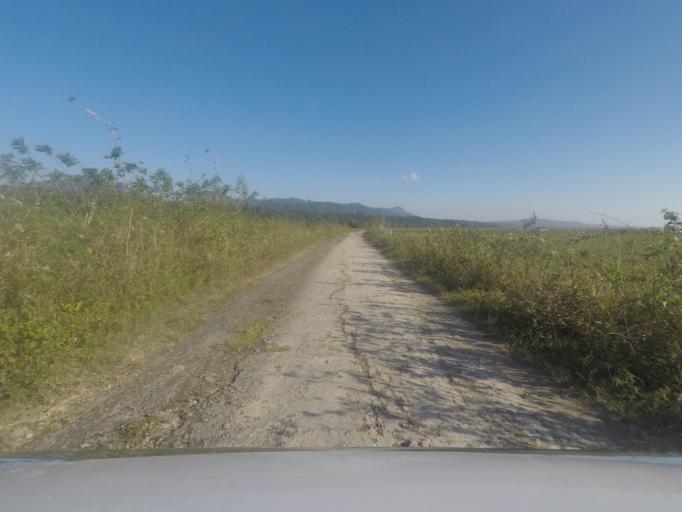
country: TL
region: Lautem
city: Lospalos
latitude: -8.4102
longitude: 127.1980
